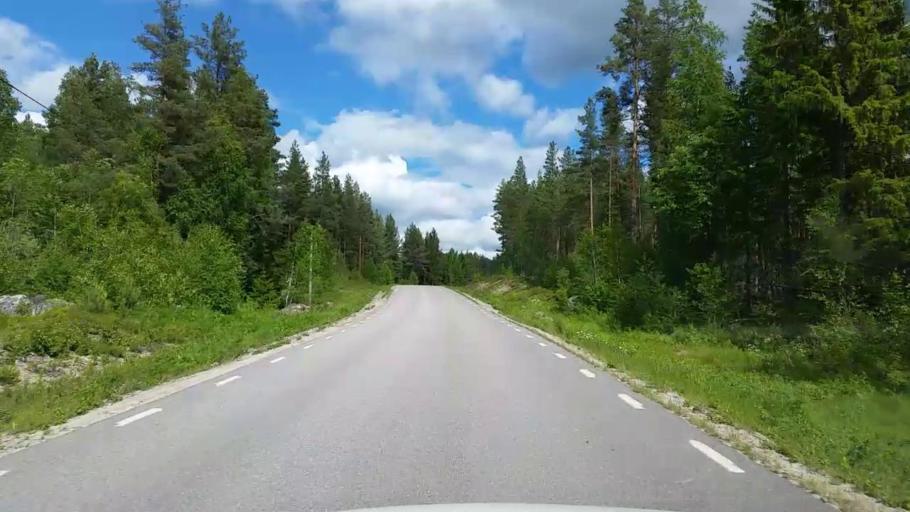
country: SE
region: Gaevleborg
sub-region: Ovanakers Kommun
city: Alfta
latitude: 61.4051
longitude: 16.0536
